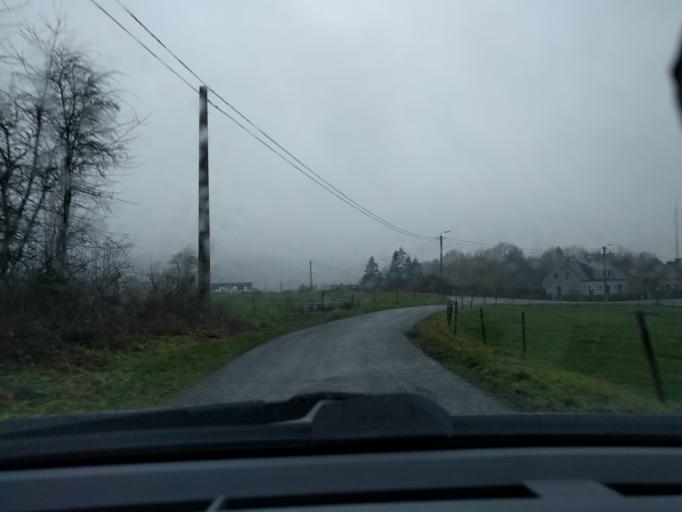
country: BE
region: Wallonia
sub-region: Province de Namur
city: Couvin
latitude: 50.0466
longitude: 4.5090
